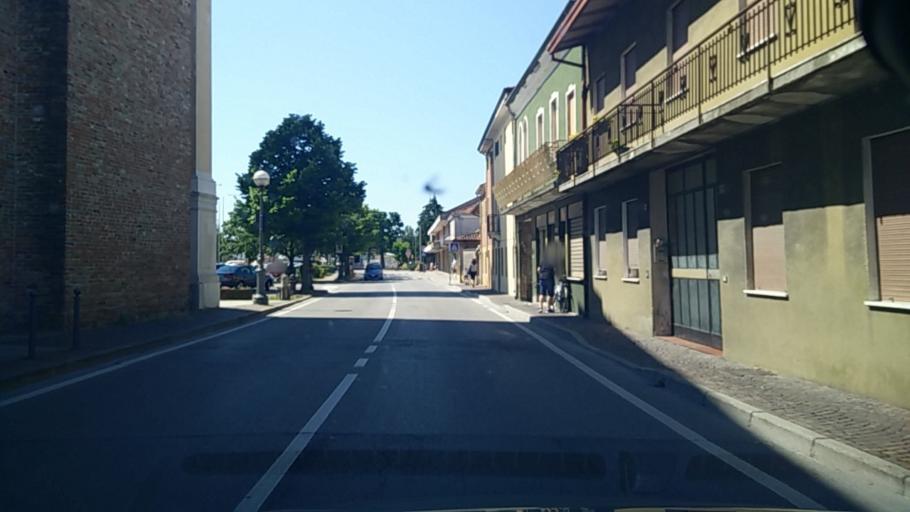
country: IT
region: Veneto
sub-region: Provincia di Venezia
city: Camponogara
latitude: 45.3858
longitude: 12.0721
